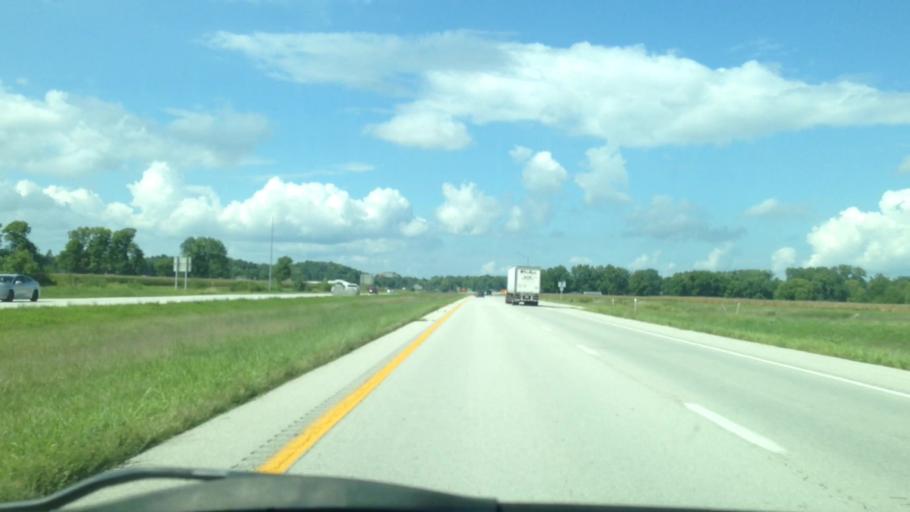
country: US
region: Illinois
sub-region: Adams County
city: Quincy
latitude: 39.9186
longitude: -91.5240
